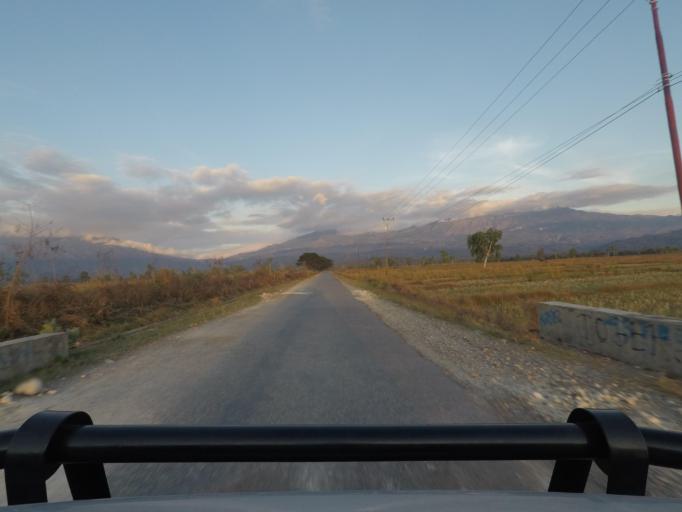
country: TL
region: Bobonaro
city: Maliana
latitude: -8.9864
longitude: 125.1633
